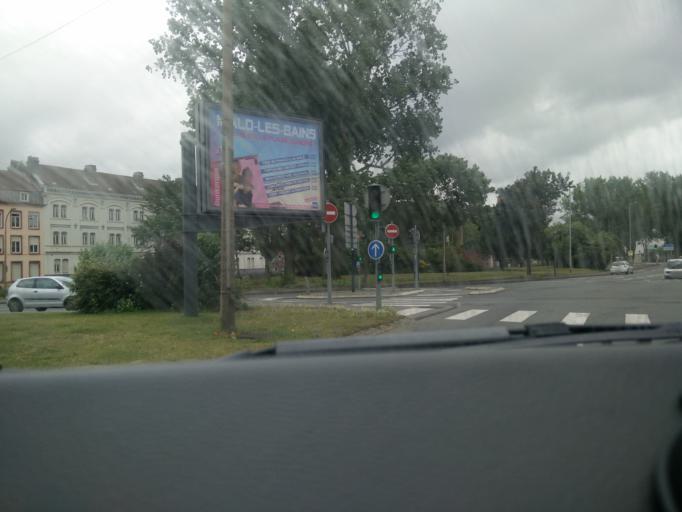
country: FR
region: Nord-Pas-de-Calais
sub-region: Departement du Nord
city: Dunkerque
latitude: 51.0319
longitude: 2.3709
